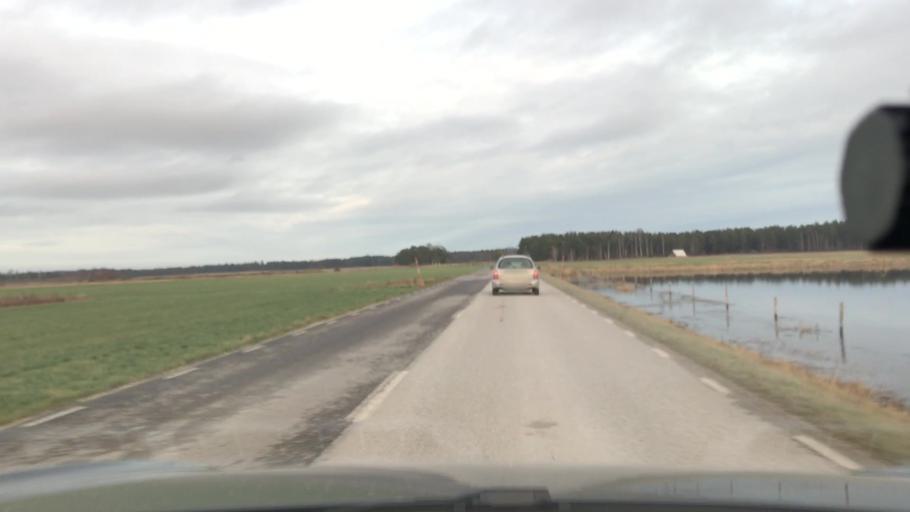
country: SE
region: Gotland
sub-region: Gotland
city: Slite
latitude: 57.7131
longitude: 18.5459
